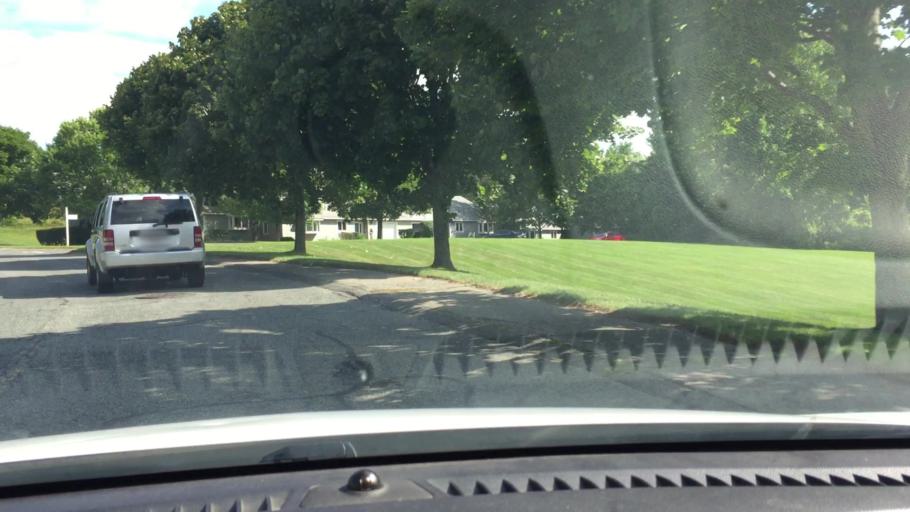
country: US
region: Massachusetts
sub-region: Berkshire County
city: Pittsfield
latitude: 42.4540
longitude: -73.2799
